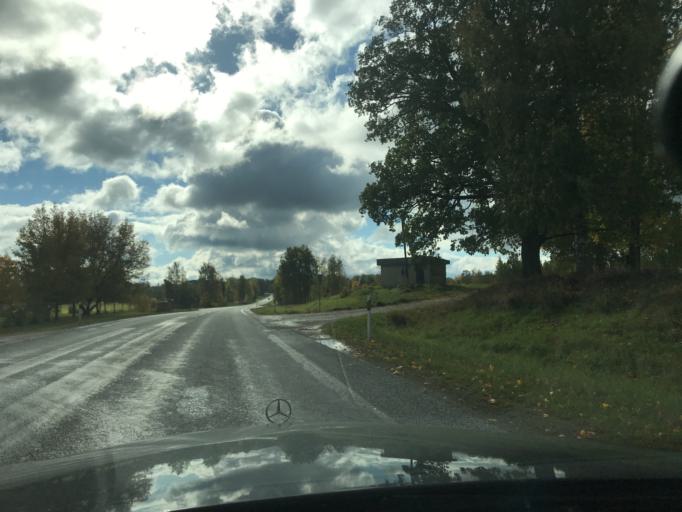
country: RU
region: Pskov
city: Pechory
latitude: 57.6906
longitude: 27.3278
